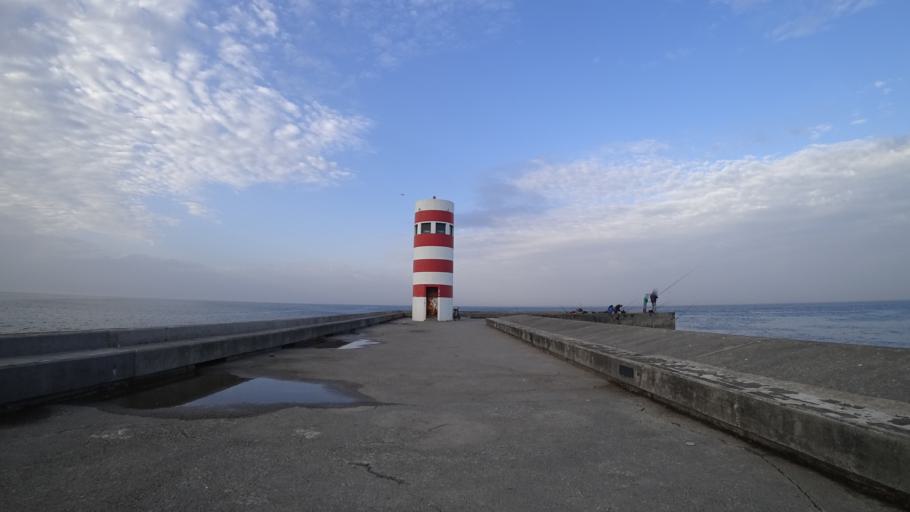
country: PT
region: Porto
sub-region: Vila Nova de Gaia
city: Canidelo
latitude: 41.1449
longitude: -8.6793
